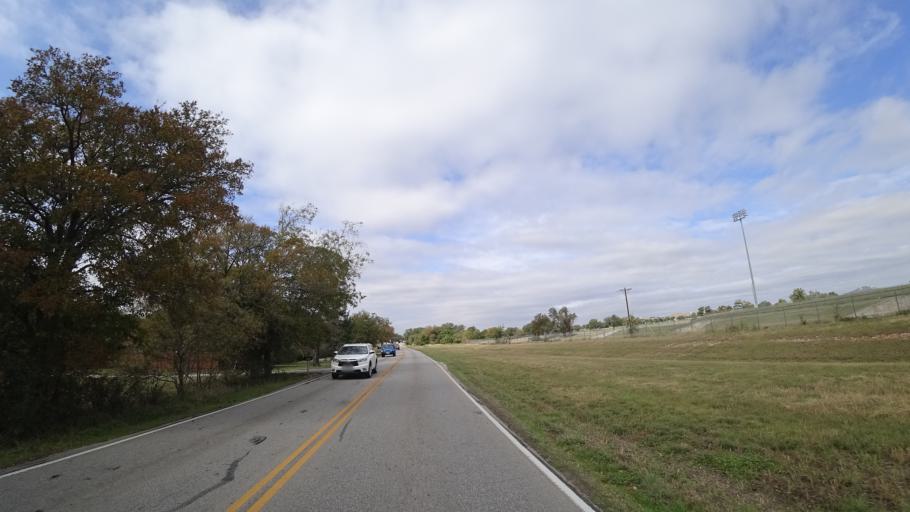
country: US
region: Texas
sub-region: Williamson County
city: Brushy Creek
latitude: 30.5324
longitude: -97.7351
